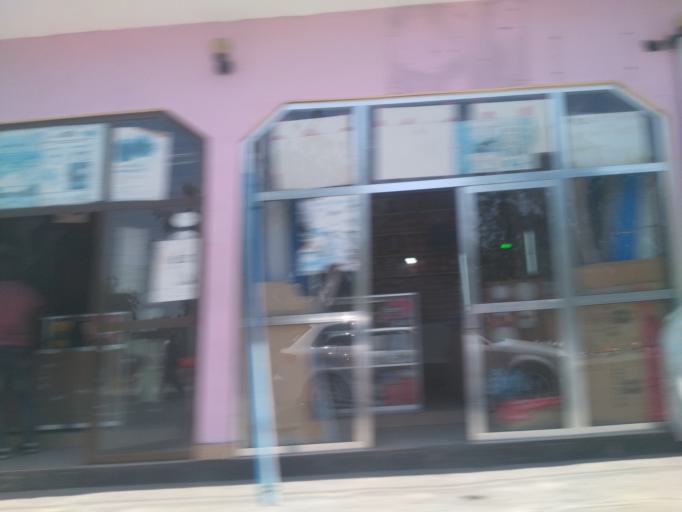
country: TZ
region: Dodoma
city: Dodoma
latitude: -6.1798
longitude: 35.7432
